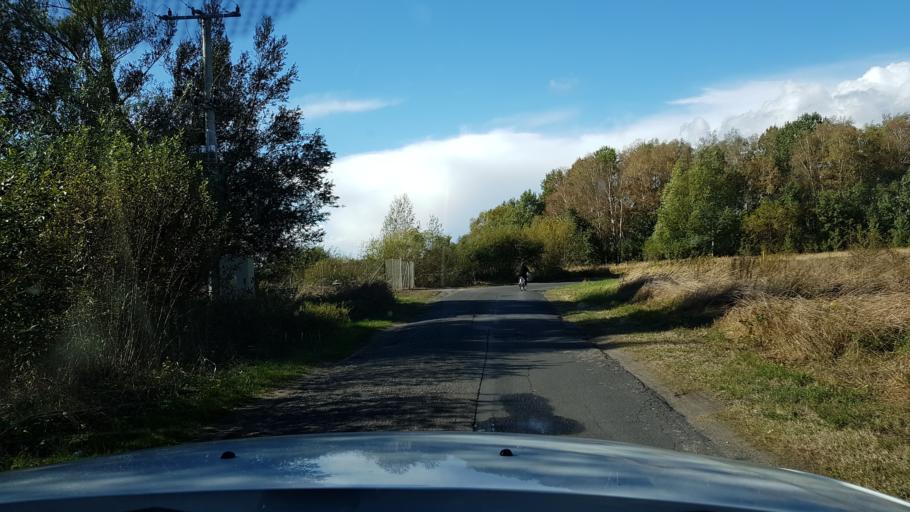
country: PL
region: West Pomeranian Voivodeship
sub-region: Powiat gryfinski
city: Gryfino
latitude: 53.2715
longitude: 14.4985
